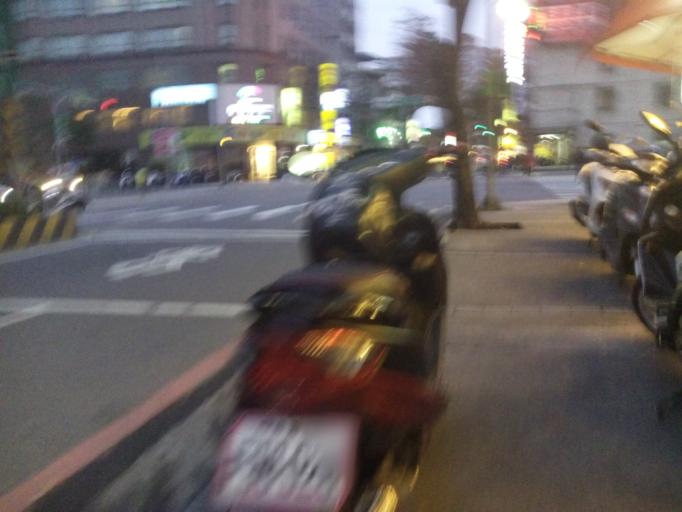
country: TW
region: Taipei
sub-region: Taipei
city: Banqiao
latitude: 24.9819
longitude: 121.4201
